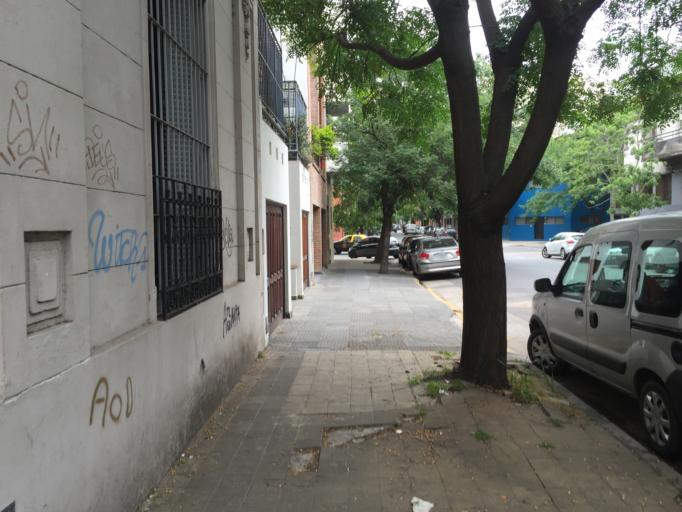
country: AR
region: Buenos Aires F.D.
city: Colegiales
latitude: -34.5865
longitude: -58.4431
